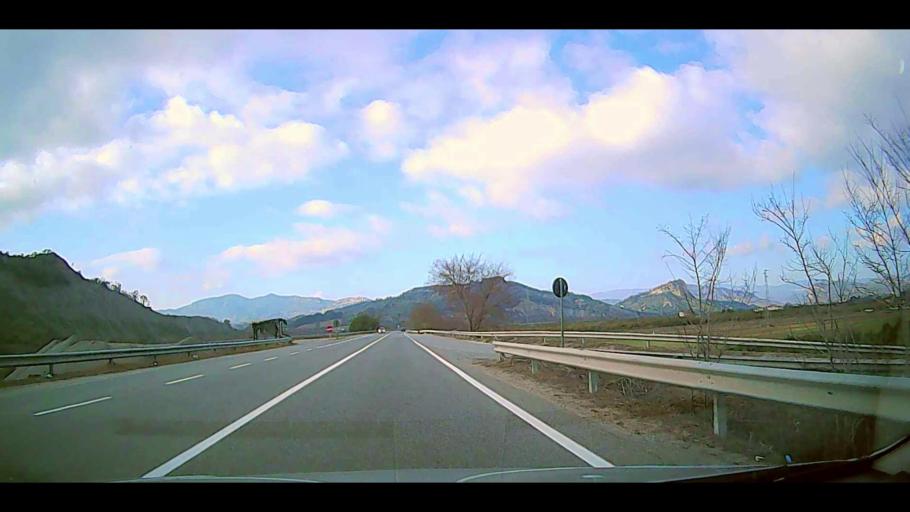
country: IT
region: Calabria
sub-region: Provincia di Crotone
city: Scandale
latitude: 39.1667
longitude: 16.9601
